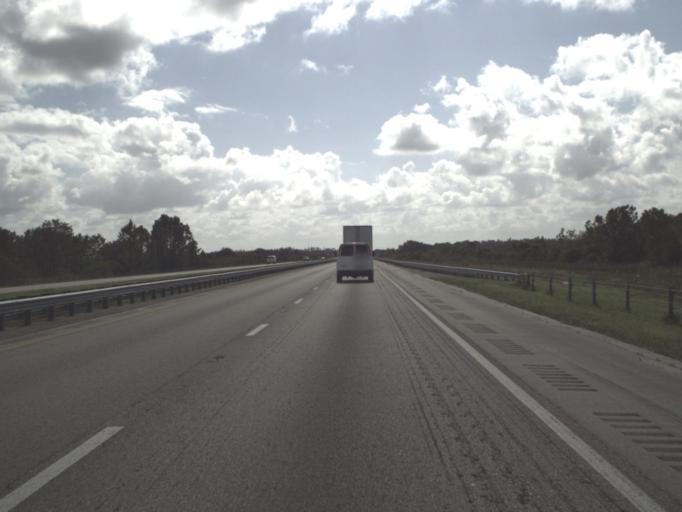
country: US
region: Florida
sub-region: Osceola County
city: Saint Cloud
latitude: 27.9404
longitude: -81.0767
